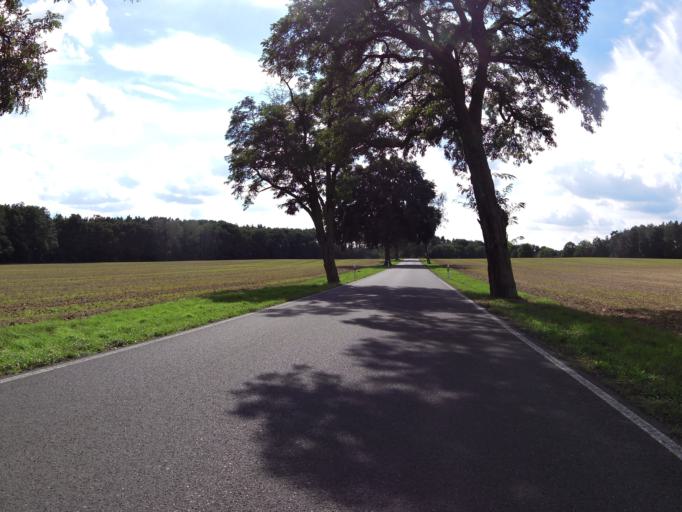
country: DE
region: Brandenburg
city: Munchehofe
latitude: 52.2058
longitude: 13.8643
